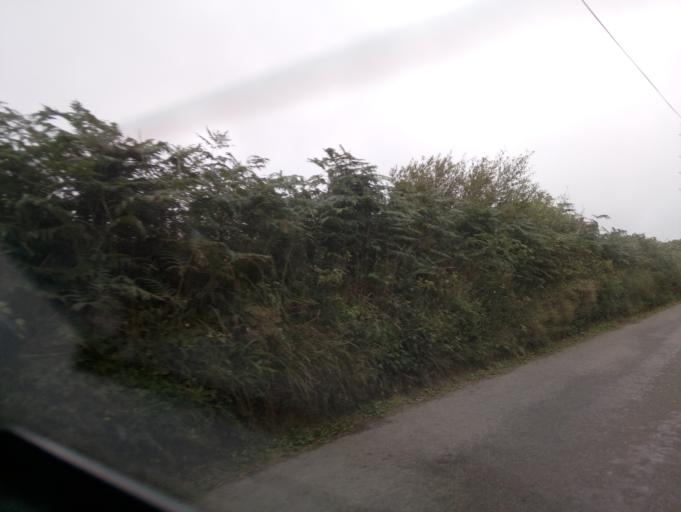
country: GB
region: England
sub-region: Devon
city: Kingsbridge
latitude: 50.3225
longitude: -3.6983
